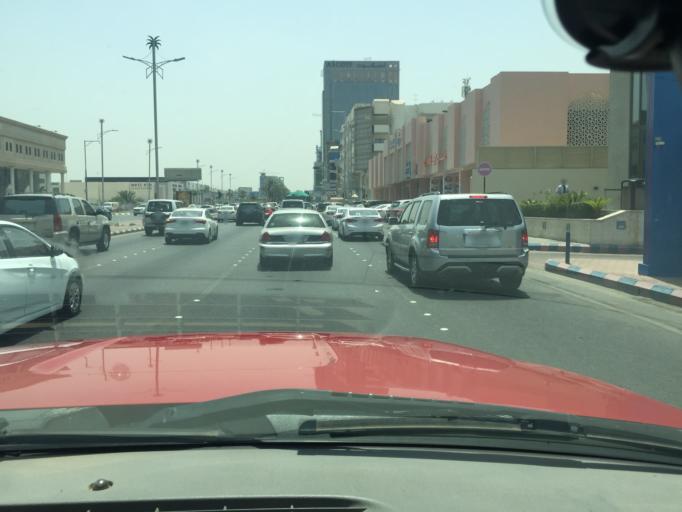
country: SA
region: Makkah
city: Jeddah
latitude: 21.5540
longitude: 39.1674
